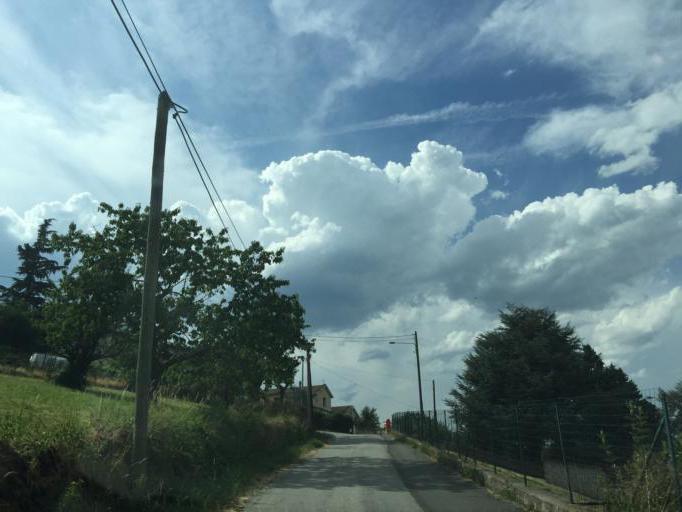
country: FR
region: Rhone-Alpes
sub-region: Departement de la Loire
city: Saint-Chamond
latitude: 45.4853
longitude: 4.4908
